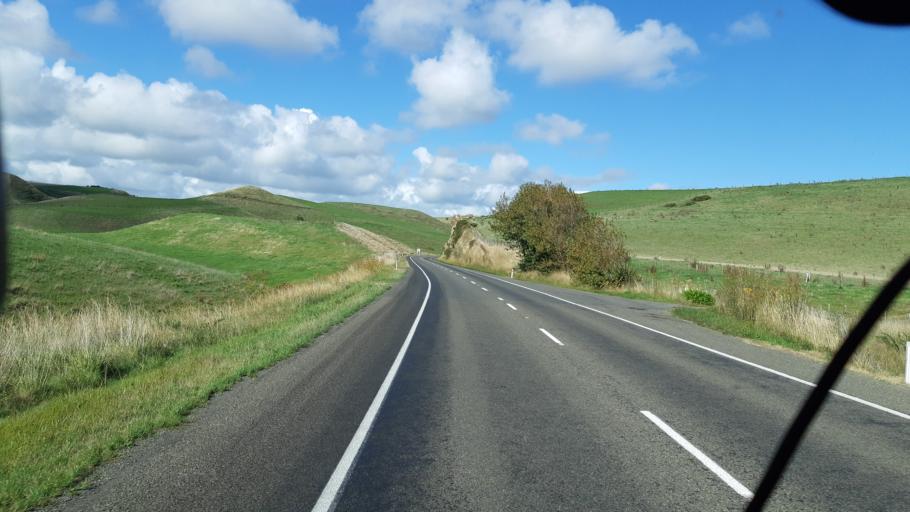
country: NZ
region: Manawatu-Wanganui
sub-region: Wanganui District
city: Wanganui
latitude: -40.0168
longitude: 175.1744
